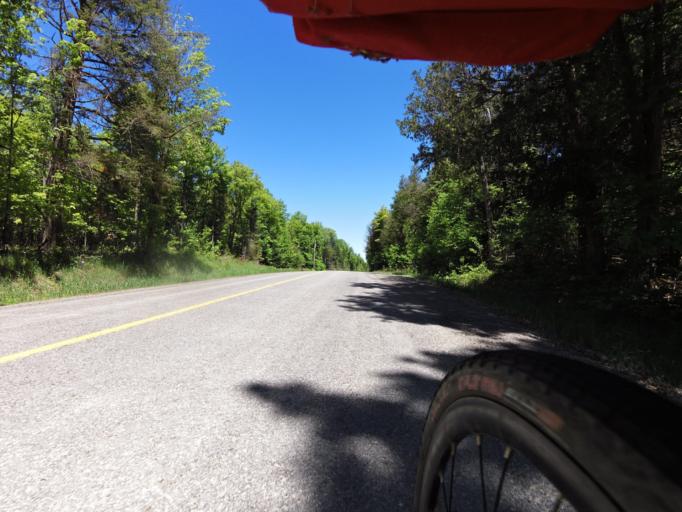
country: CA
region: Ontario
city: Carleton Place
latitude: 45.1727
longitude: -76.4120
